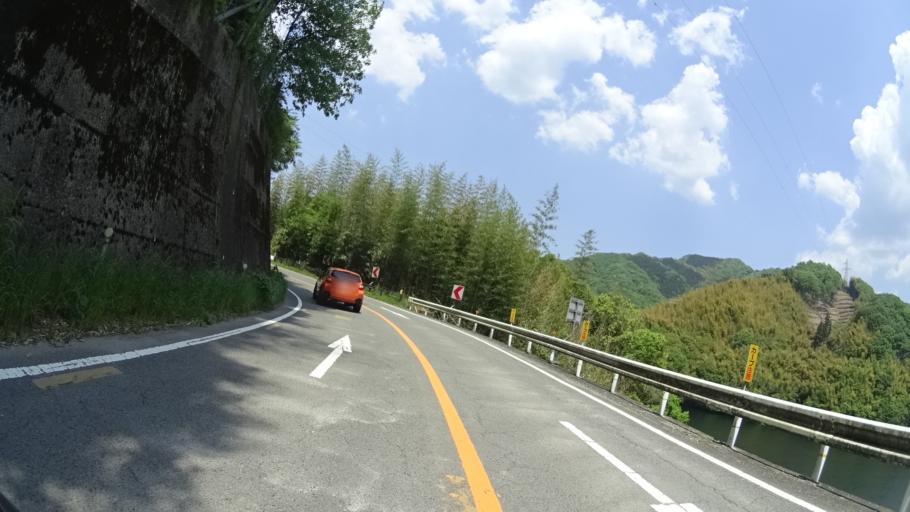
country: JP
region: Ehime
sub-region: Shikoku-chuo Shi
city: Matsuyama
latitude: 33.8819
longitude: 132.8370
